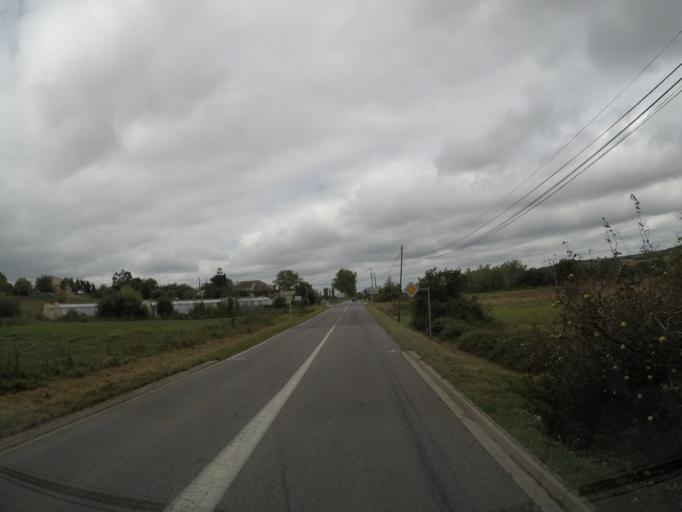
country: FR
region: Midi-Pyrenees
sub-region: Departement de l'Ariege
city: Lezat-sur-Leze
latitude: 43.2318
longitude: 1.3754
